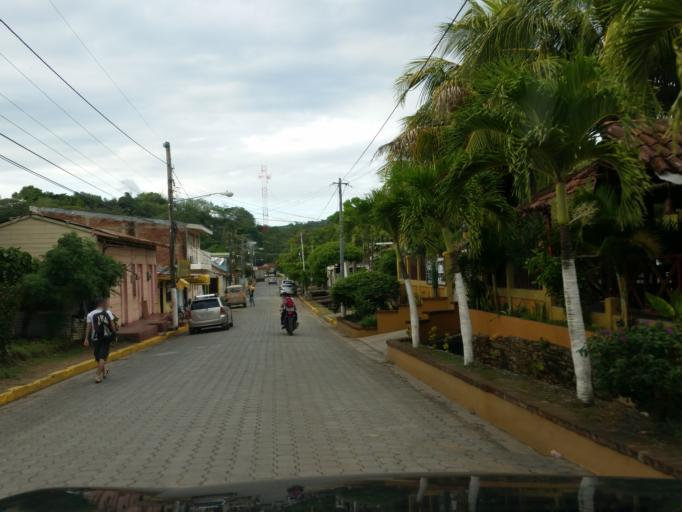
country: NI
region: Rivas
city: San Juan del Sur
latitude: 11.2537
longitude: -85.8696
